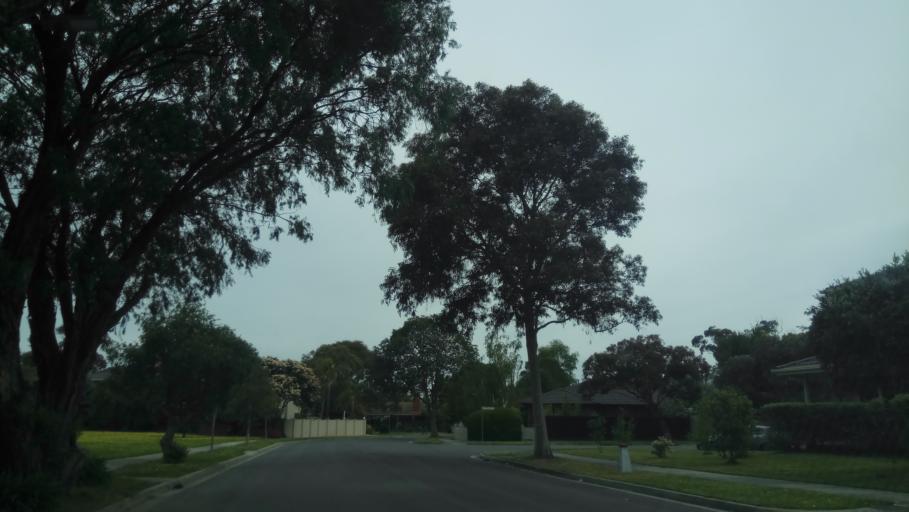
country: AU
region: Victoria
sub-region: Kingston
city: Dingley Village
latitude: -37.9743
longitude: 145.1316
